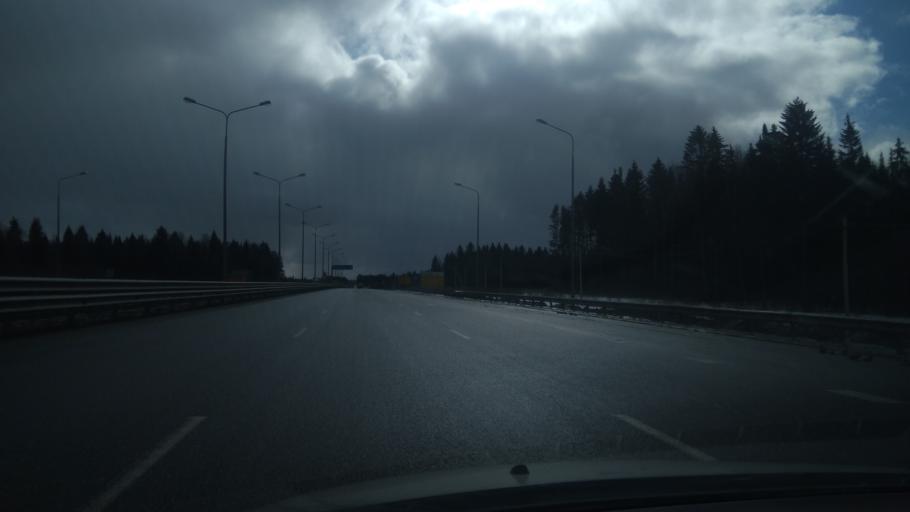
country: RU
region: Perm
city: Kukushtan
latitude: 57.6306
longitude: 56.4627
